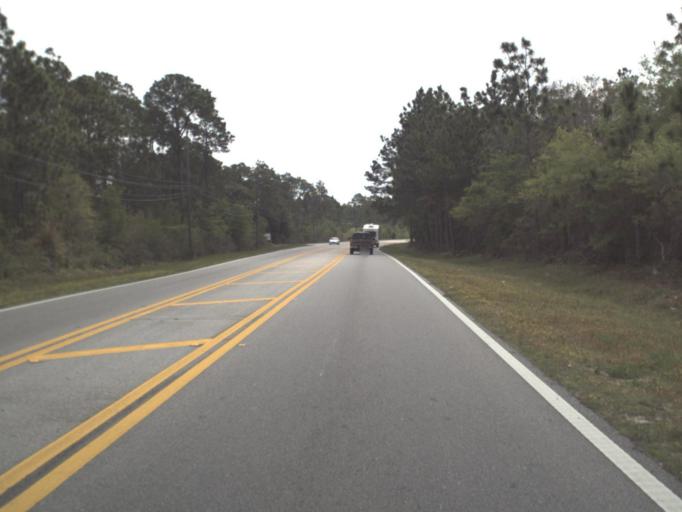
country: US
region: Florida
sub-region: Escambia County
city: Myrtle Grove
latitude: 30.3625
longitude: -87.3537
